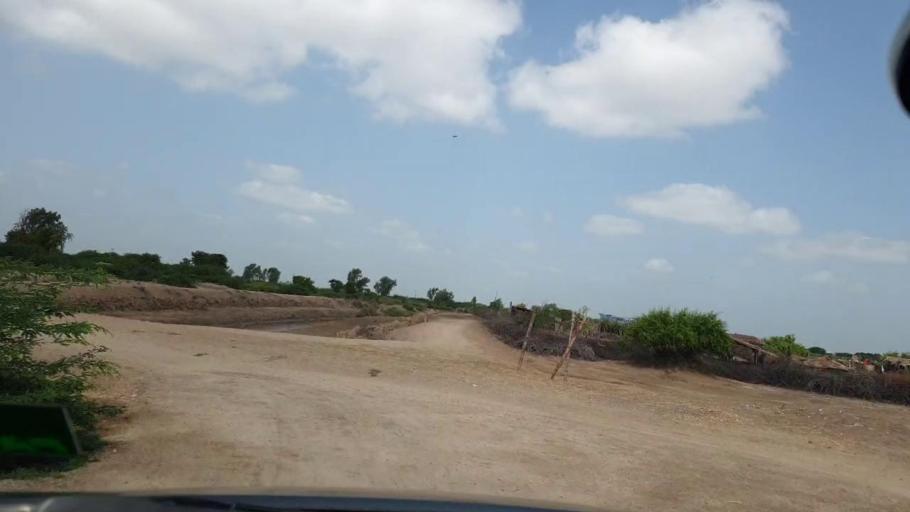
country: PK
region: Sindh
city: Kadhan
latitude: 24.6044
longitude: 69.1192
